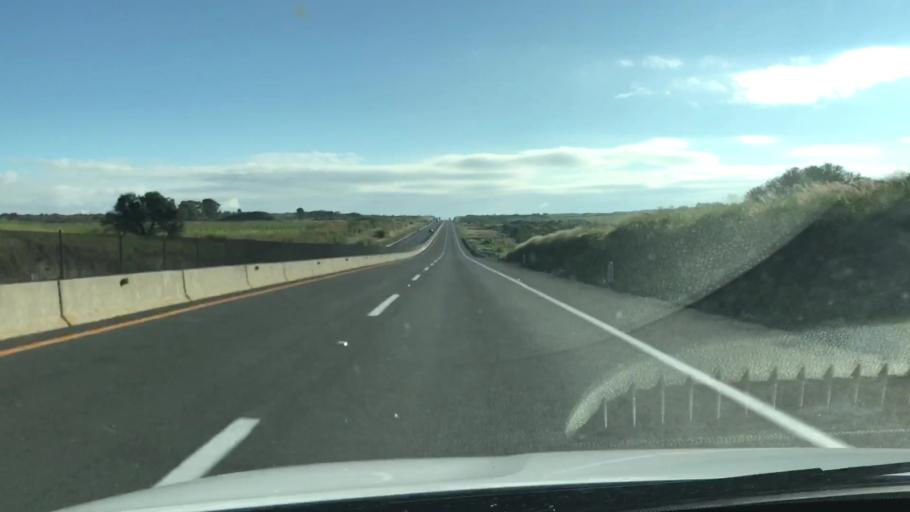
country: MX
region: Jalisco
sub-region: San Juan de los Lagos
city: Colonia Santa Cecilia (La Sauceda)
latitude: 21.1787
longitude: -102.3764
